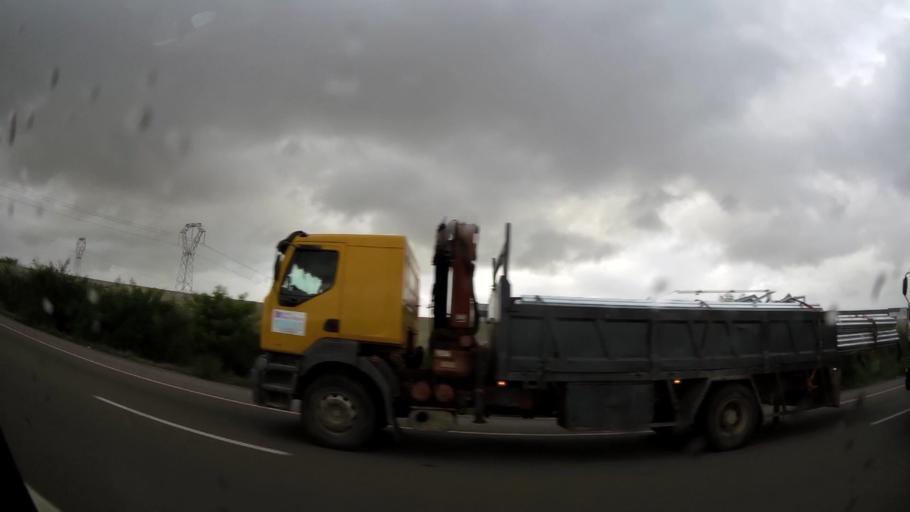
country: MA
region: Grand Casablanca
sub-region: Mohammedia
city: Mohammedia
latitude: 33.6548
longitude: -7.4127
